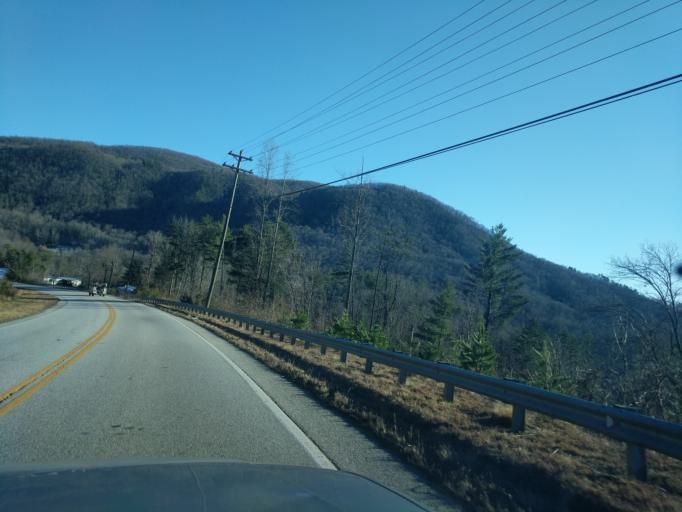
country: US
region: Georgia
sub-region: Rabun County
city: Clayton
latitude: 34.8627
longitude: -83.5186
